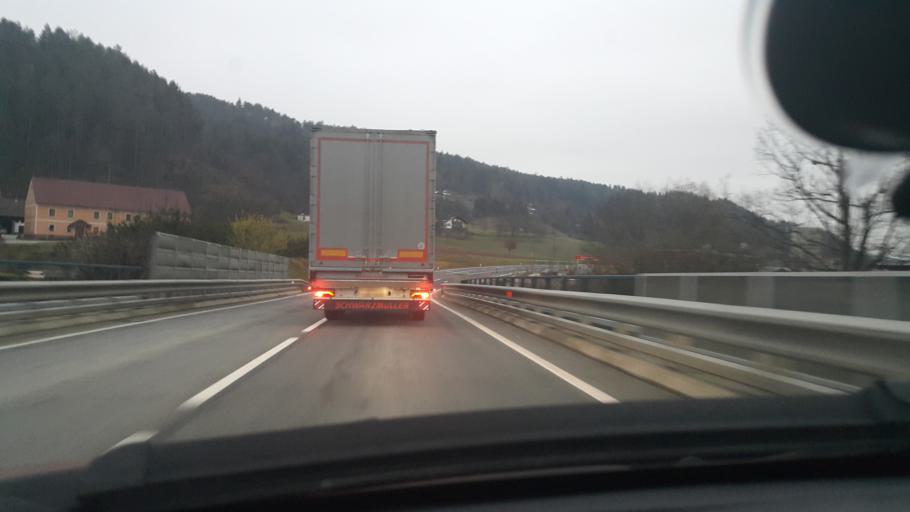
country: AT
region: Carinthia
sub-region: Politischer Bezirk Volkermarkt
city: Ruden
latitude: 46.6506
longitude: 14.7684
